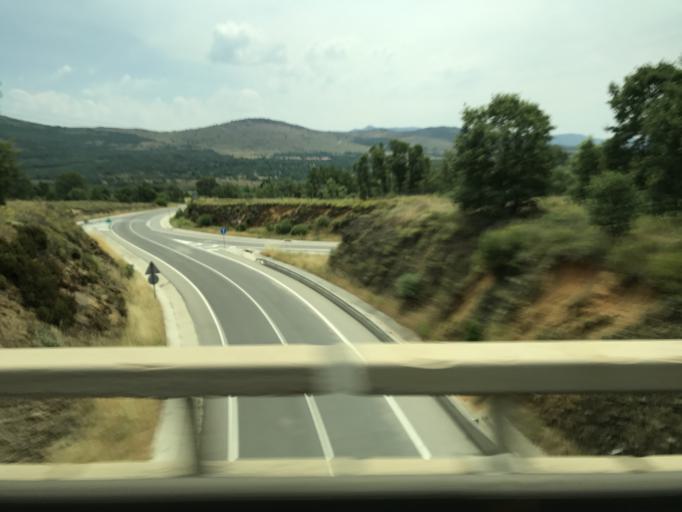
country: ES
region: Madrid
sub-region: Provincia de Madrid
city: Horcajo de la Sierra
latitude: 41.0797
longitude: -3.5999
